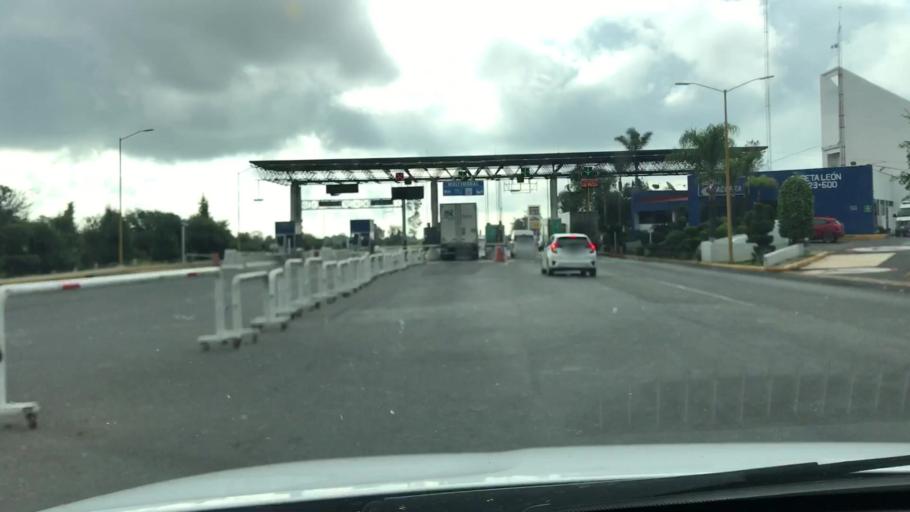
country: MX
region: Guanajuato
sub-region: Leon
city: Centro Familiar la Soledad
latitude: 21.1032
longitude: -101.7851
